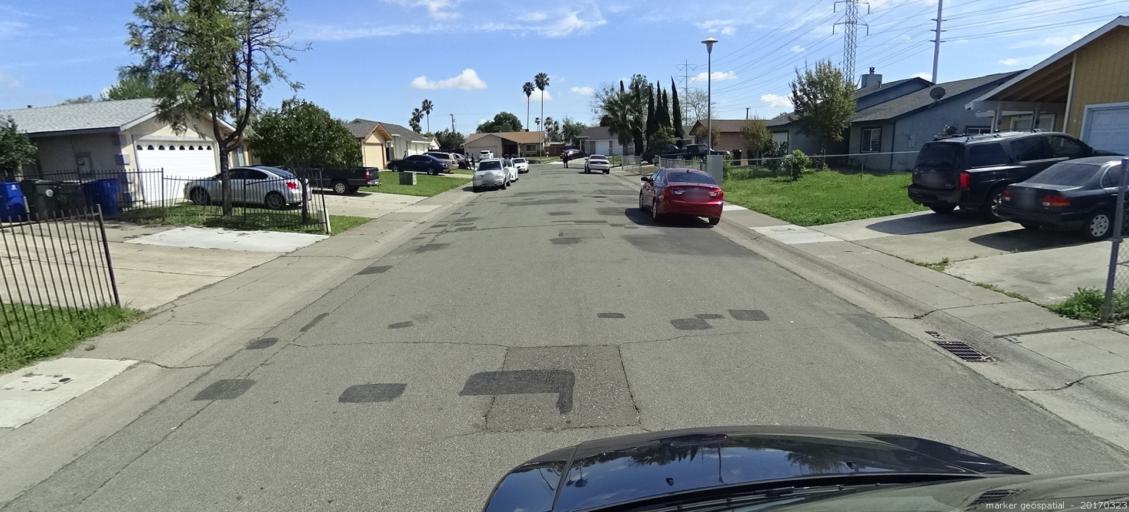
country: US
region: California
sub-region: Sacramento County
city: Florin
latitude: 38.5091
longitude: -121.4185
